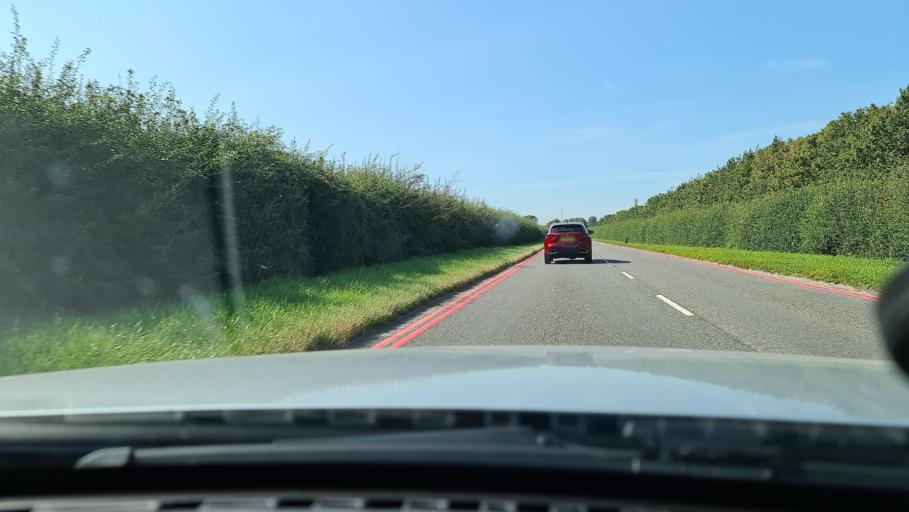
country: GB
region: England
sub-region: Leicestershire
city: Castle Donington
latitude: 52.8244
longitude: -1.3144
